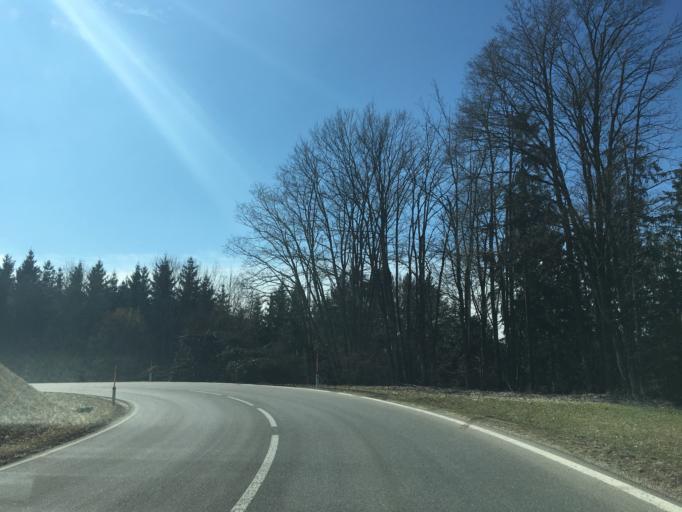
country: AT
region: Upper Austria
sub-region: Politischer Bezirk Perg
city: Sankt Georgen am Walde
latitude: 48.2874
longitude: 14.8983
